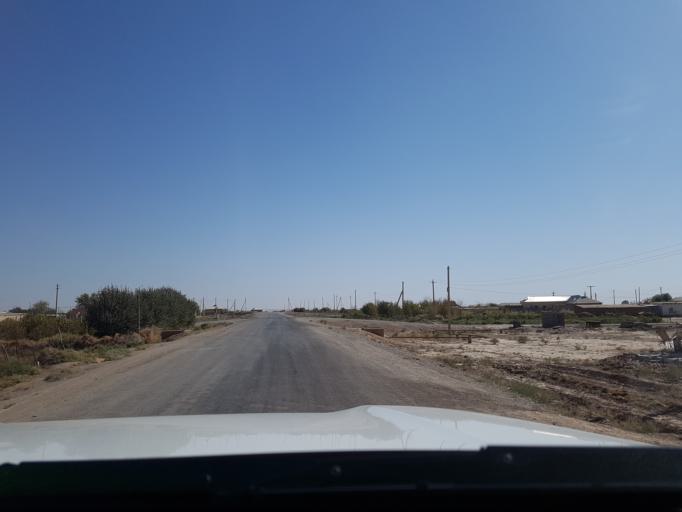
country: IR
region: Razavi Khorasan
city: Sarakhs
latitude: 36.5182
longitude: 61.2511
